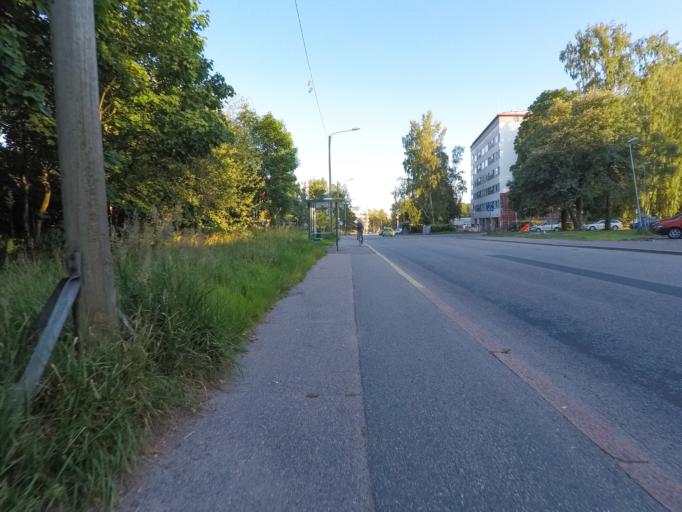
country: FI
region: Uusimaa
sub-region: Helsinki
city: Vantaa
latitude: 60.2037
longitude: 25.0593
